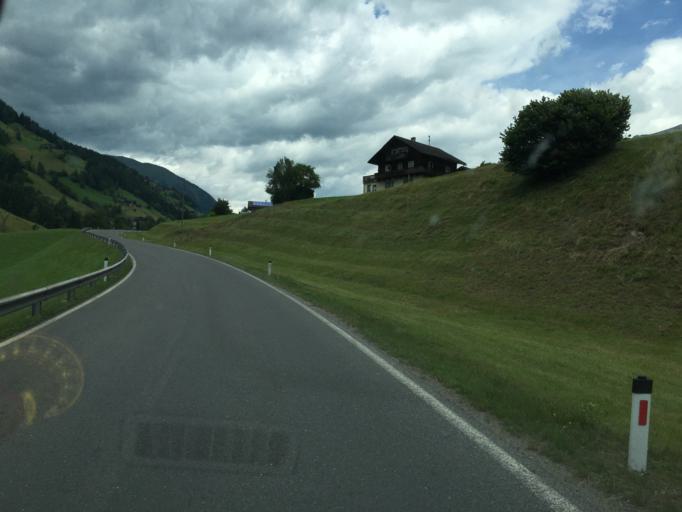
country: AT
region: Carinthia
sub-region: Politischer Bezirk Spittal an der Drau
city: Grosskirchheim
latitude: 46.9526
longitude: 12.8992
